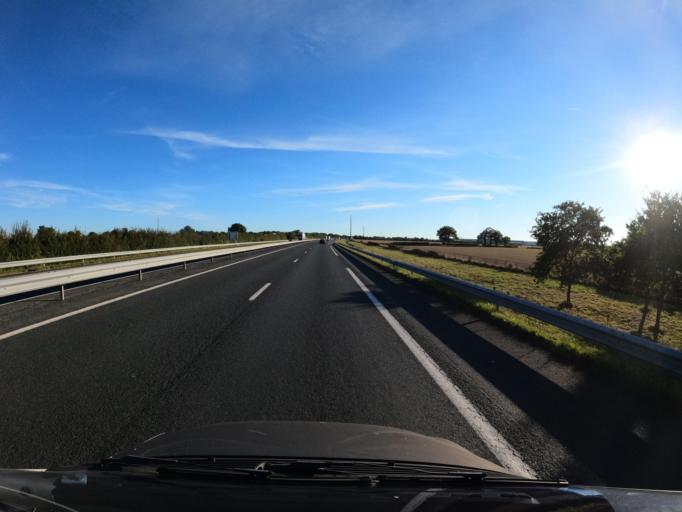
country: FR
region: Pays de la Loire
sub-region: Departement de Maine-et-Loire
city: Mazieres-en-Mauges
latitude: 47.0705
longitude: -0.8264
